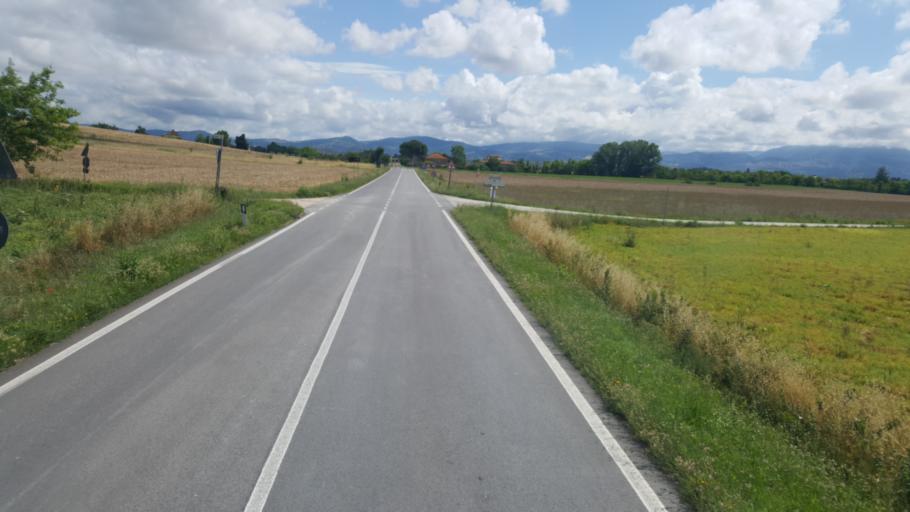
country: IT
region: Umbria
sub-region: Provincia di Perugia
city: Bettona
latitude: 43.0427
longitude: 12.4797
